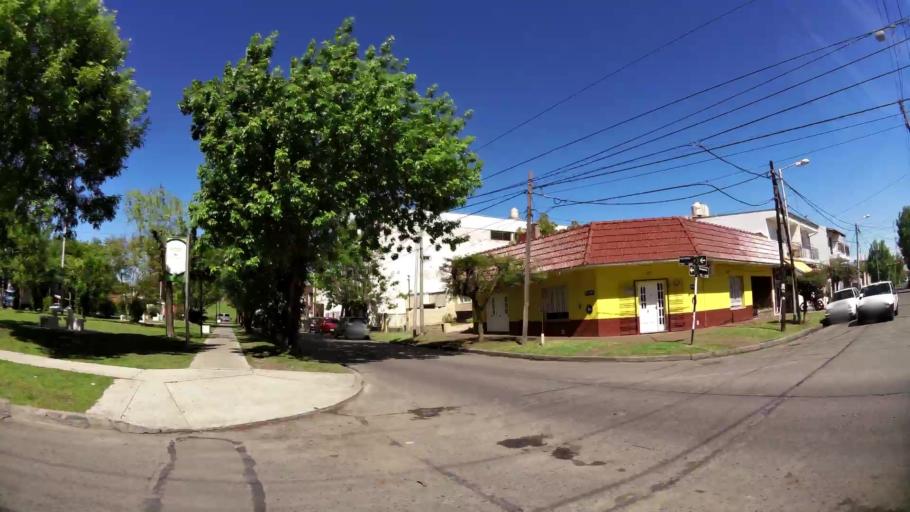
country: AR
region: Buenos Aires
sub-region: Partido de Quilmes
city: Quilmes
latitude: -34.6938
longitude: -58.3059
